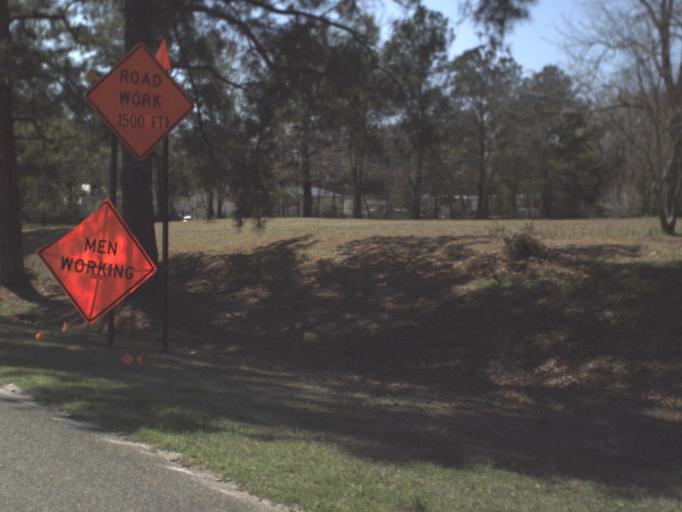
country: US
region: Florida
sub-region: Calhoun County
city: Blountstown
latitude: 30.5356
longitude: -85.0286
